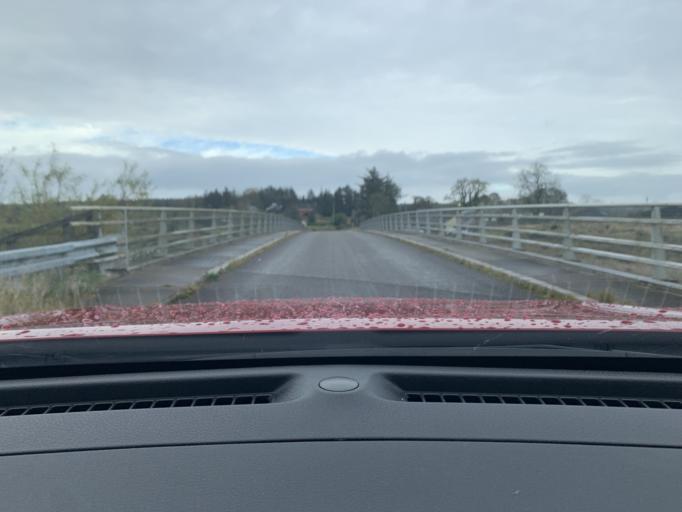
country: IE
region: Connaught
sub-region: Roscommon
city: Ballaghaderreen
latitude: 53.9151
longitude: -8.5664
